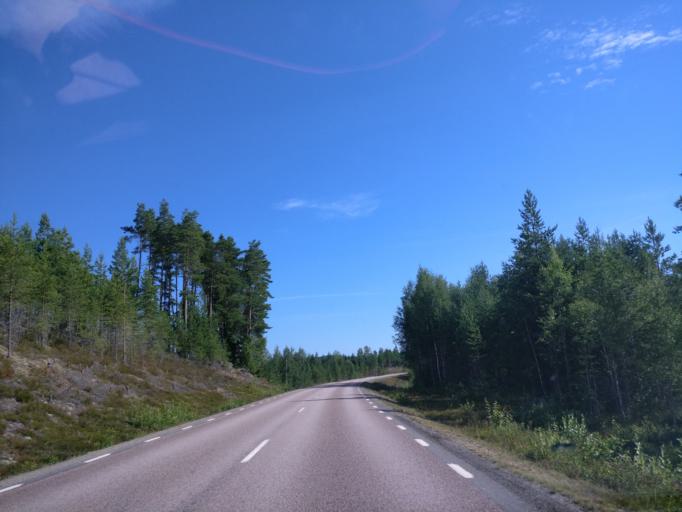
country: SE
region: Vaermland
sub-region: Hagfors Kommun
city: Hagfors
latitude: 60.0384
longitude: 13.9219
